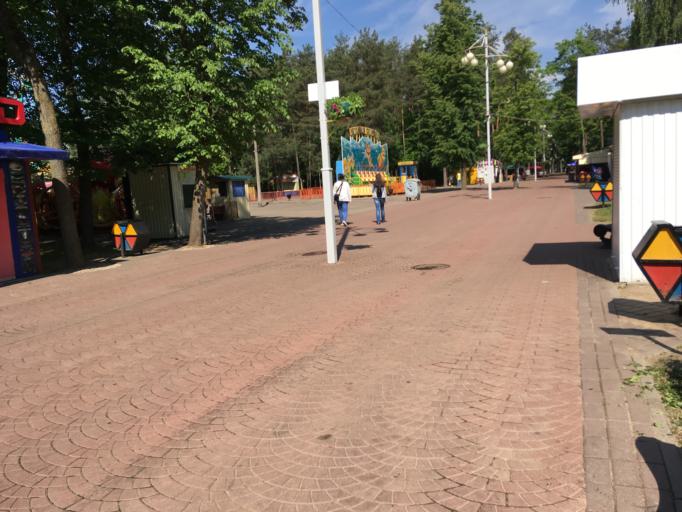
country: BY
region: Minsk
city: Minsk
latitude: 53.9198
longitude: 27.6150
